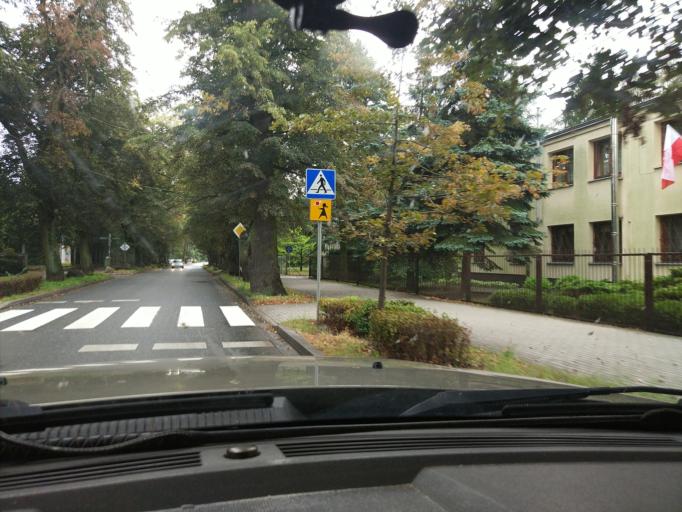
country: PL
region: Masovian Voivodeship
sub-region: Powiat grodziski
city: Podkowa Lesna
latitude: 52.1213
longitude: 20.7264
